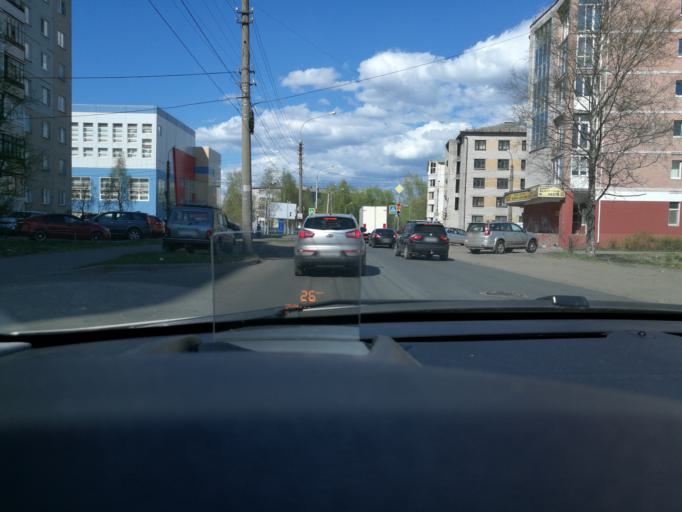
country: RU
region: Arkhangelskaya
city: Arkhangel'sk
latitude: 64.5541
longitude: 40.5381
